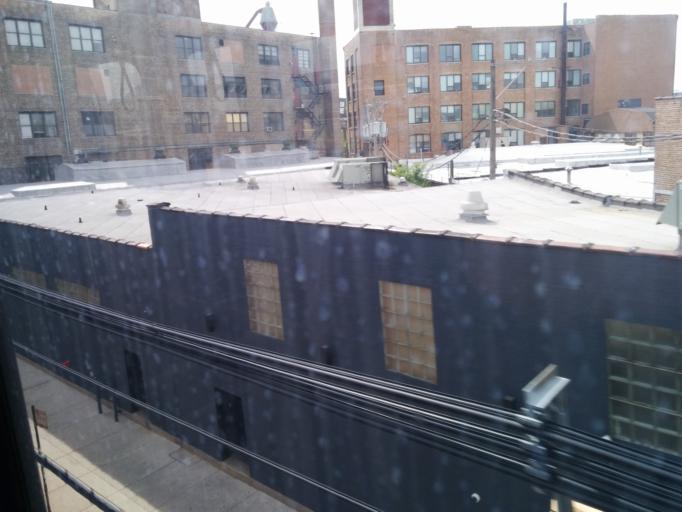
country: US
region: Illinois
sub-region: Cook County
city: Chicago
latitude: 41.8854
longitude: -87.6641
